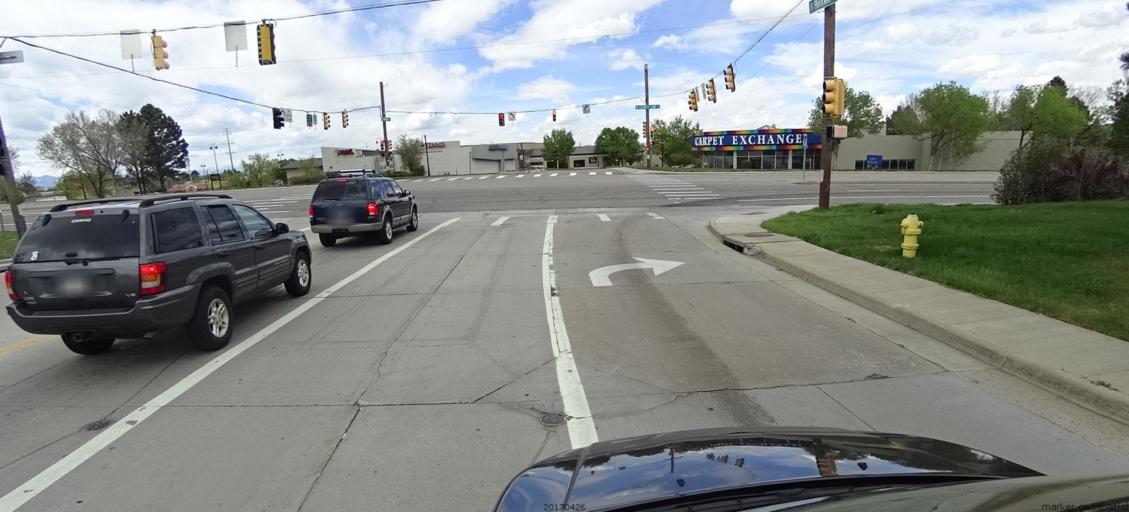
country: US
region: Colorado
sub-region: Douglas County
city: Acres Green
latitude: 39.5656
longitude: -104.9022
